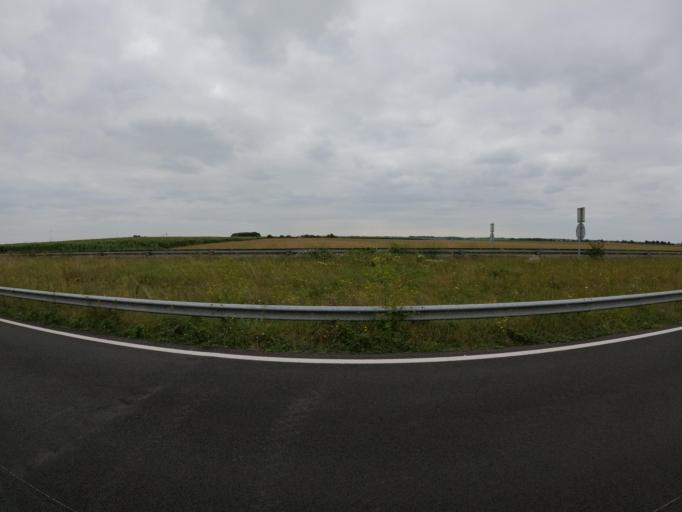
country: FR
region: Pays de la Loire
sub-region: Departement de la Vendee
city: Maillezais
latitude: 46.4238
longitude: -0.7150
